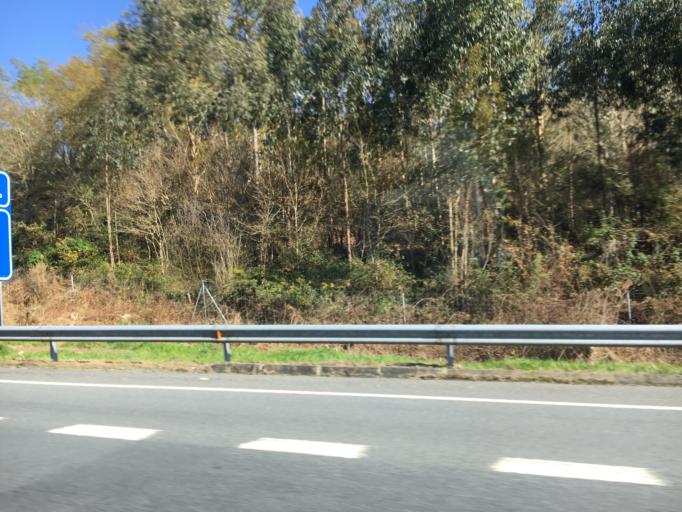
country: ES
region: Galicia
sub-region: Provincia da Coruna
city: Coiros
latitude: 43.2440
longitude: -8.1563
